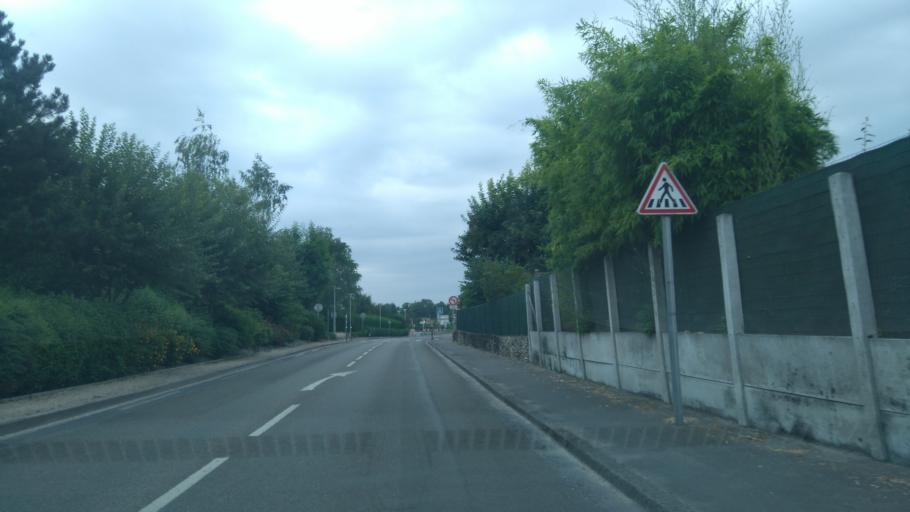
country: FR
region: Picardie
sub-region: Departement de l'Oise
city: Saint-Maximin
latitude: 49.2223
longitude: 2.4551
